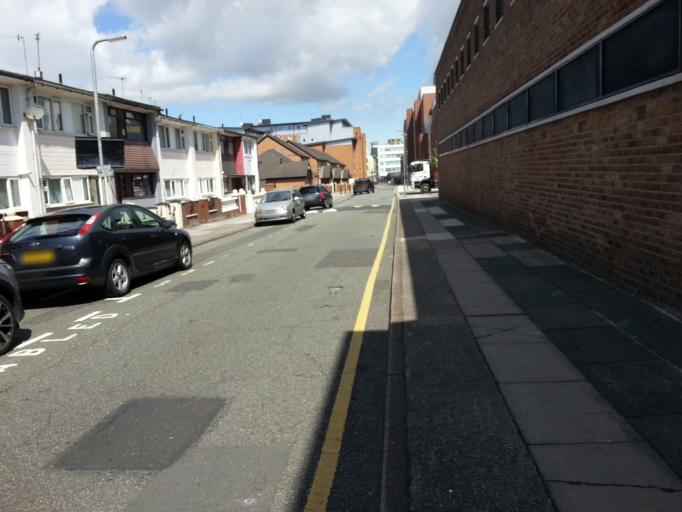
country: GB
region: England
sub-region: Liverpool
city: Liverpool
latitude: 53.4067
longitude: -2.9699
